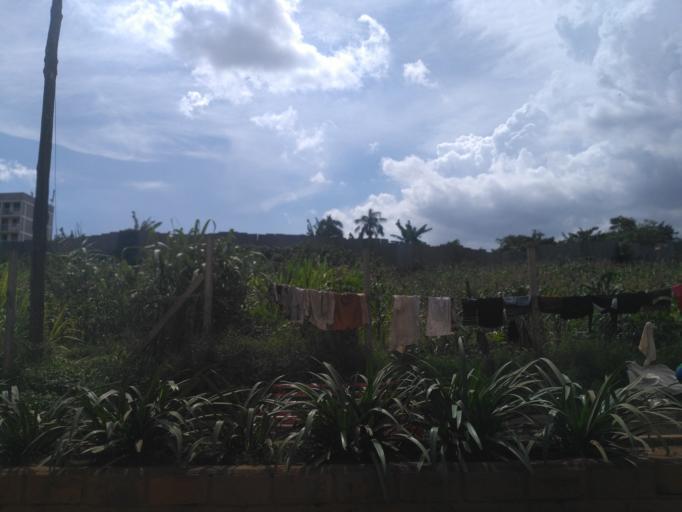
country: UG
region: Central Region
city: Kampala Central Division
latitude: 0.3413
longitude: 32.5711
